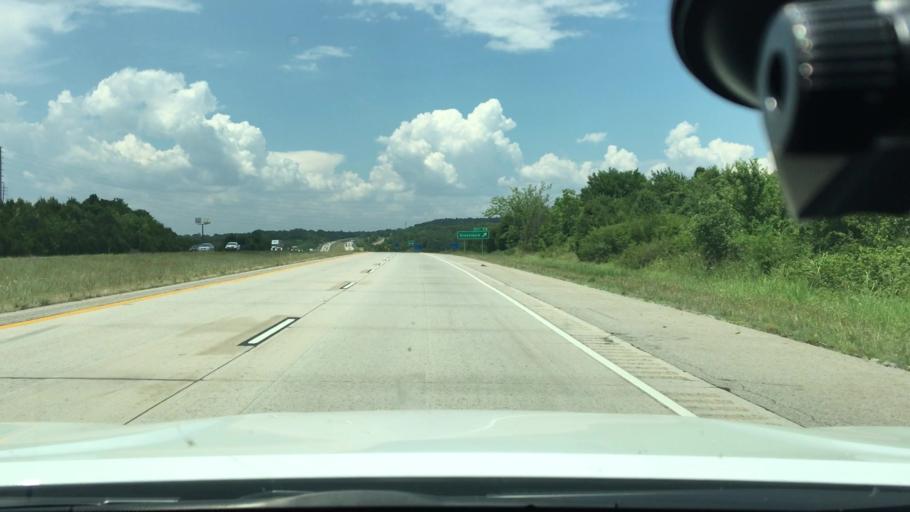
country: US
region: Arkansas
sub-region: Washington County
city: Greenland
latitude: 35.9912
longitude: -94.1965
